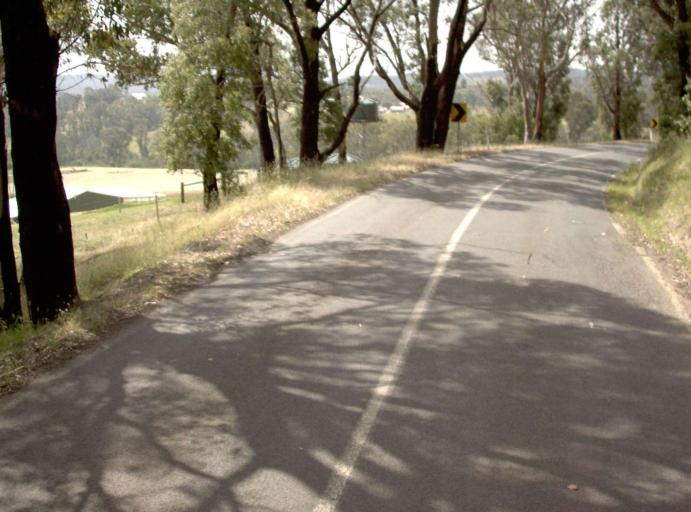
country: AU
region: Victoria
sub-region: Latrobe
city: Traralgon
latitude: -38.3215
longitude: 146.5694
